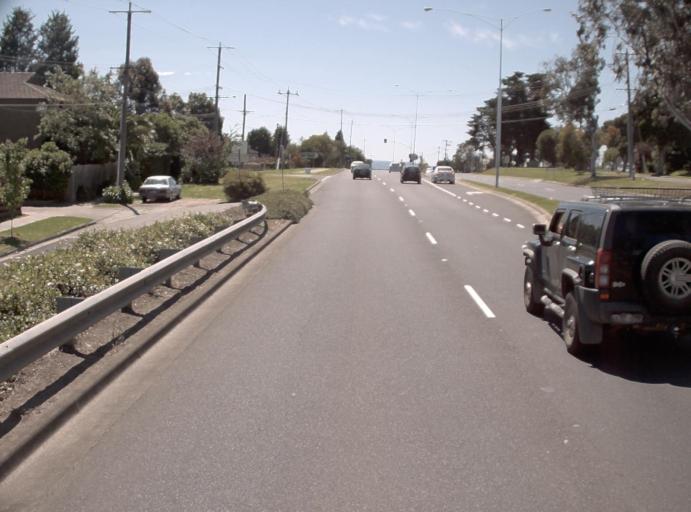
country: AU
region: Victoria
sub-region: Manningham
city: Donvale
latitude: -37.7794
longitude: 145.1636
